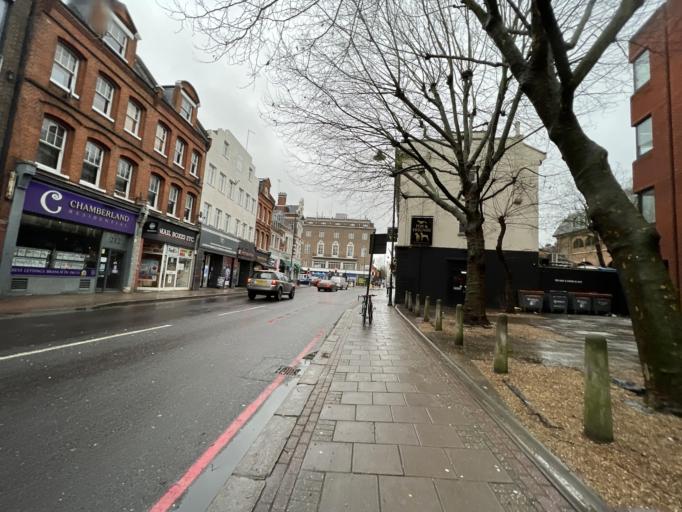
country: GB
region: England
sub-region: Greater London
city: Wandsworth
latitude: 51.4611
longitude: -0.2181
